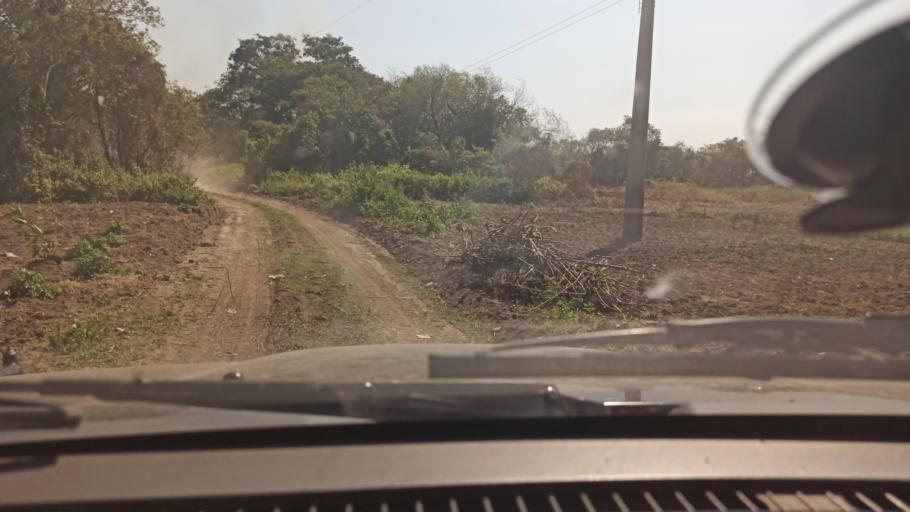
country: PY
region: Asuncion
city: Asuncion
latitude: -25.3476
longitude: -57.6703
